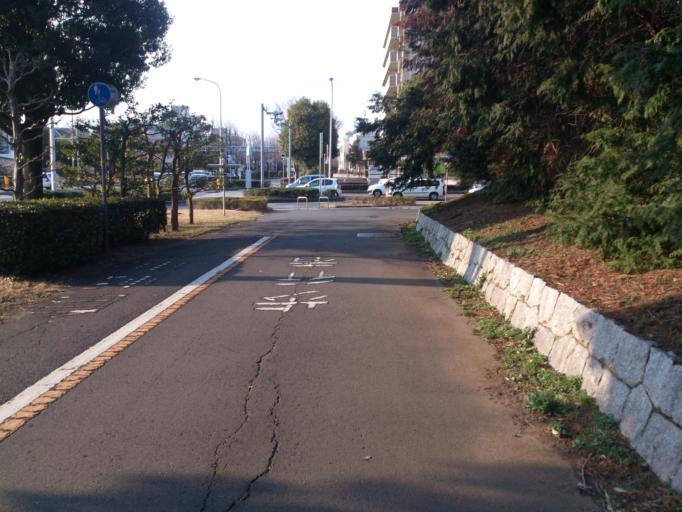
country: JP
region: Ibaraki
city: Naka
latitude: 36.0870
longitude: 140.1037
